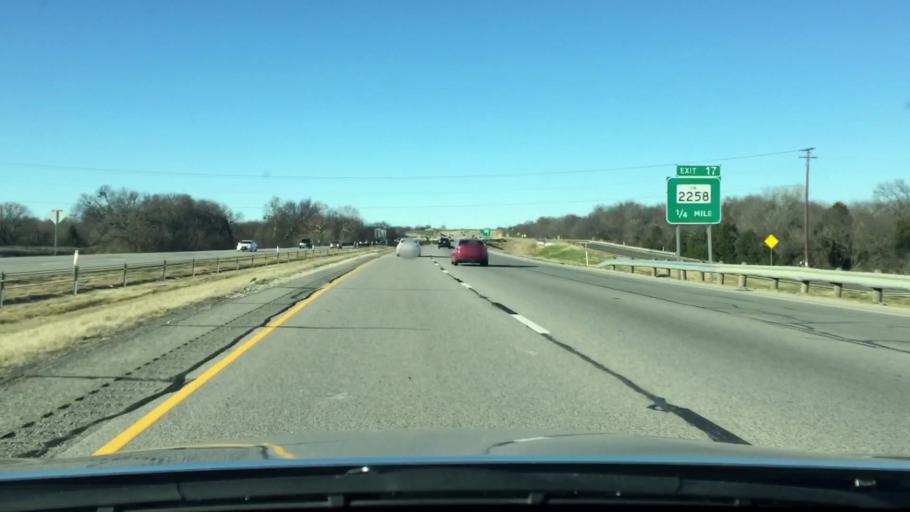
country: US
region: Texas
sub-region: Johnson County
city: Grandview
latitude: 32.2895
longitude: -97.1785
